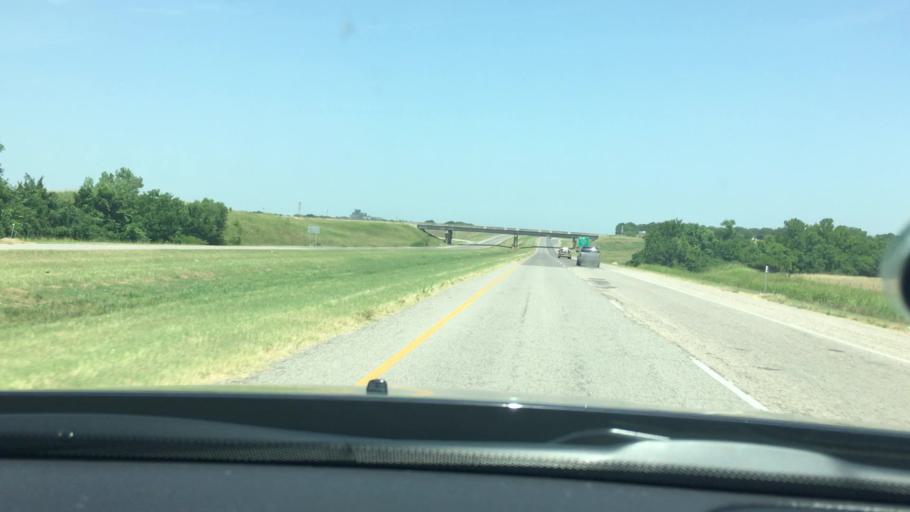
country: US
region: Oklahoma
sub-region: Pontotoc County
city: Ada
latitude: 34.7236
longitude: -96.6317
